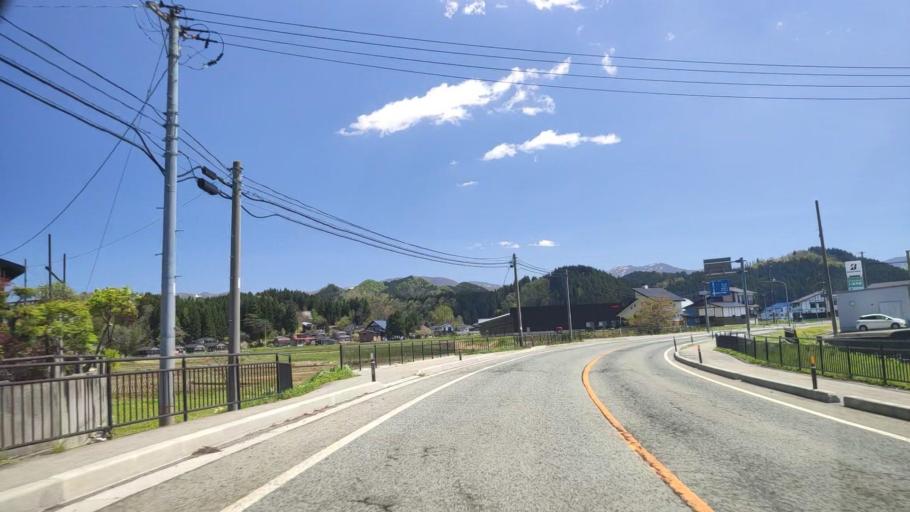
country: JP
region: Yamagata
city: Shinjo
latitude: 38.8891
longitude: 140.3305
